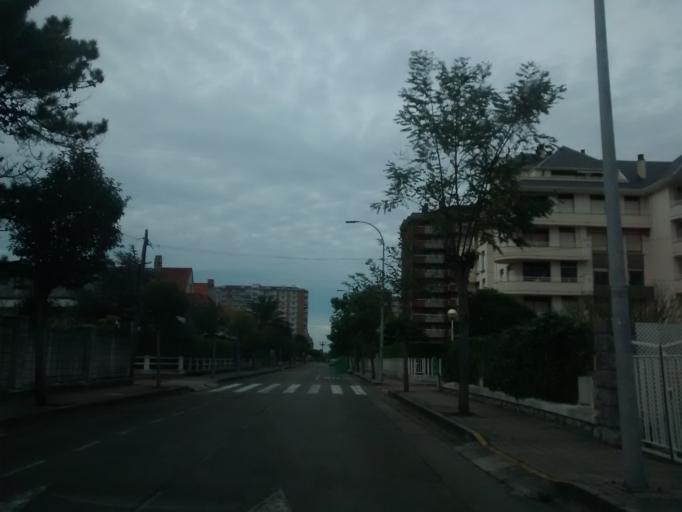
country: ES
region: Cantabria
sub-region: Provincia de Cantabria
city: Santona
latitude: 43.4230
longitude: -3.4460
